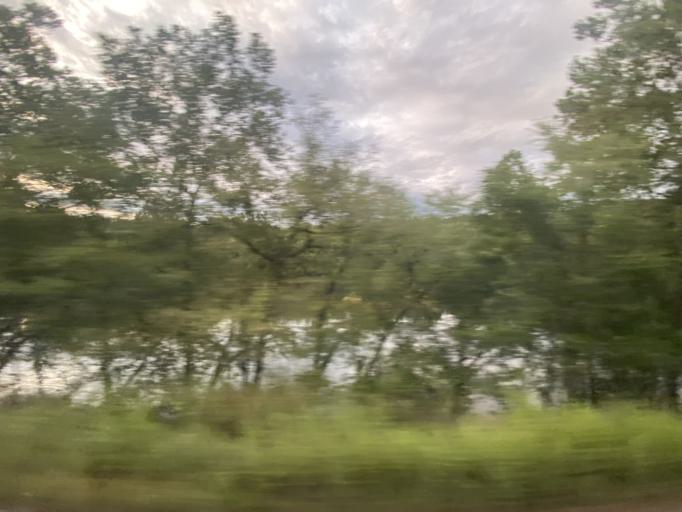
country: US
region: West Virginia
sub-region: Mineral County
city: Fort Ashby
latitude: 39.5224
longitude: -78.5395
